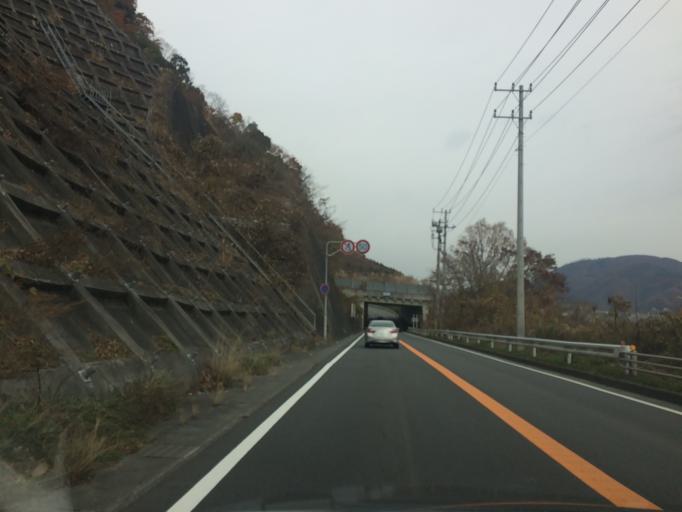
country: JP
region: Shizuoka
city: Fujinomiya
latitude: 35.3938
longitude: 138.4425
